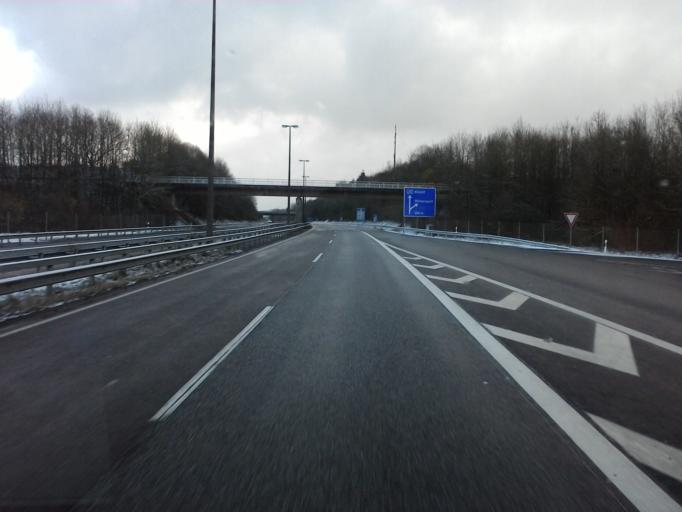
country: DE
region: Rheinland-Pfalz
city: Winterspelt
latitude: 50.2290
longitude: 6.1884
